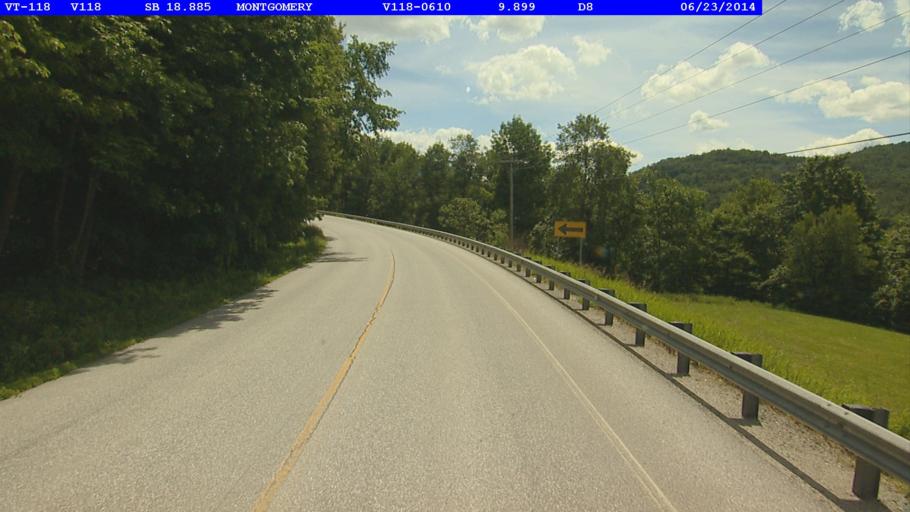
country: US
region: Vermont
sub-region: Franklin County
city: Richford
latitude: 44.9127
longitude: -72.6679
